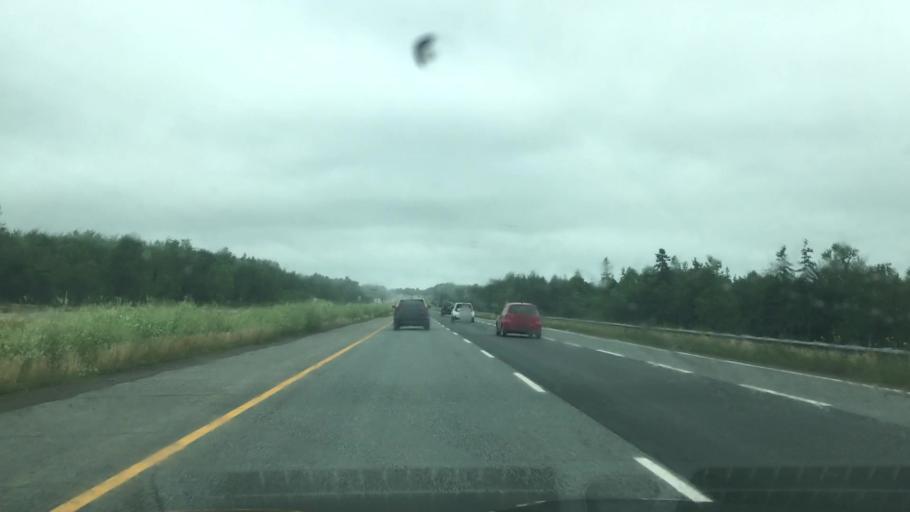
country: CA
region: Nova Scotia
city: Truro
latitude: 45.2521
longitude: -63.2920
